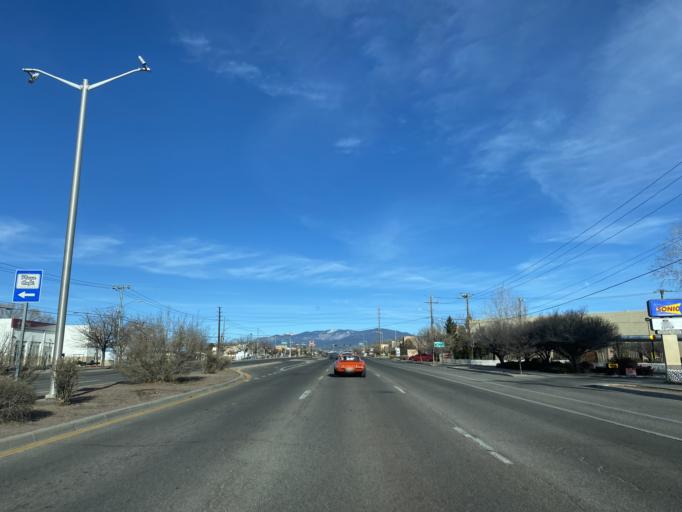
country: US
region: New Mexico
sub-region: Santa Fe County
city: Agua Fria
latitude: 35.6408
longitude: -106.0150
